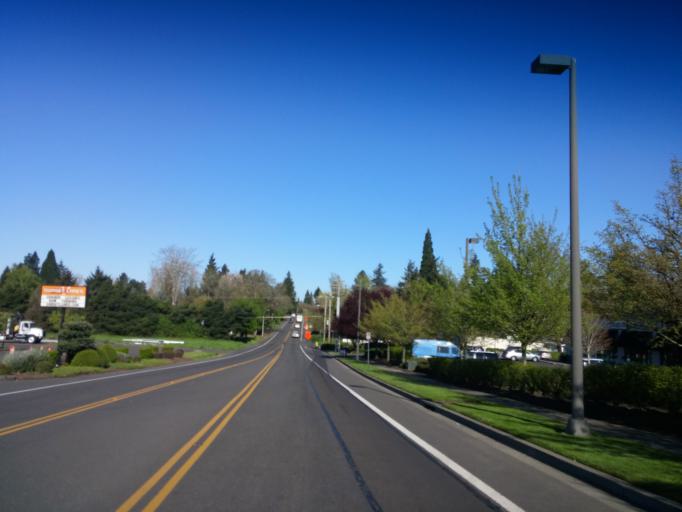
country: US
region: Oregon
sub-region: Washington County
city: Cedar Hills
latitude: 45.5021
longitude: -122.8077
